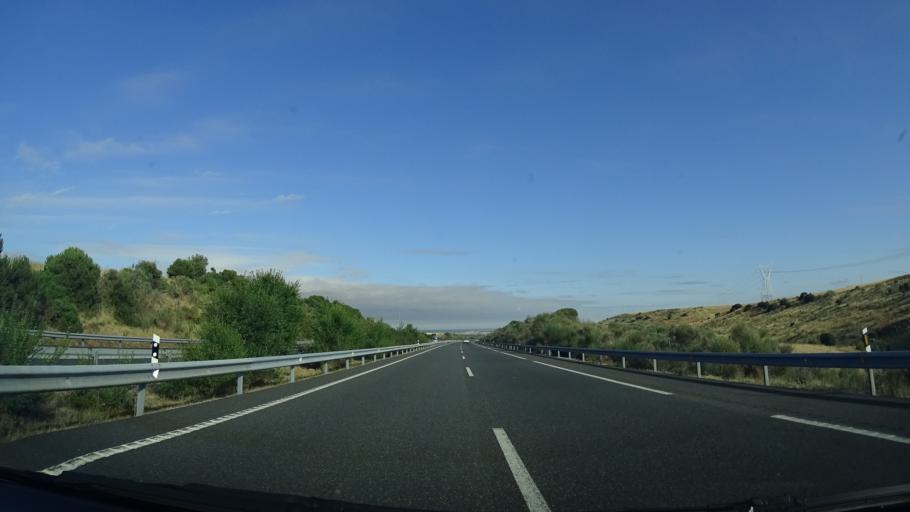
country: ES
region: Castille and Leon
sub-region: Provincia de Segovia
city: Labajos
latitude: 40.8290
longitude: -4.5216
